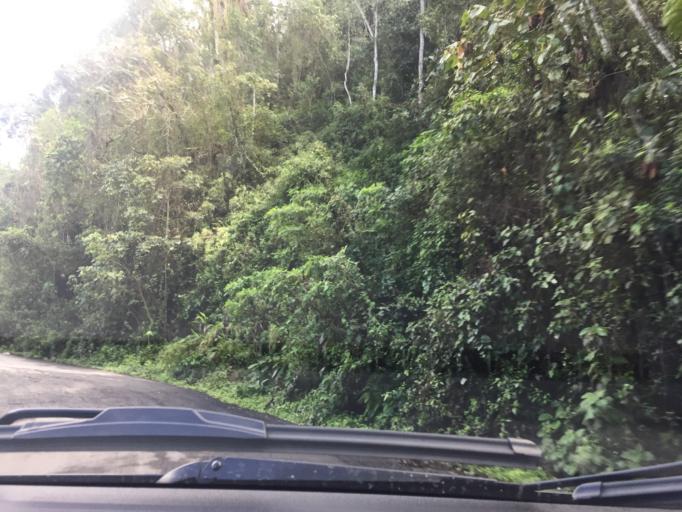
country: CO
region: Cundinamarca
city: San Francisco
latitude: 5.0242
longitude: -74.2734
